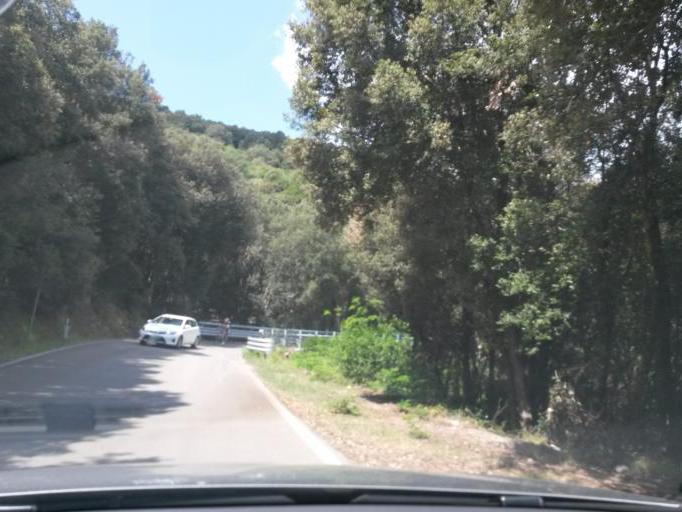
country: IT
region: Tuscany
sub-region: Provincia di Livorno
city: Campo nell'Elba
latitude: 42.7430
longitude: 10.2067
